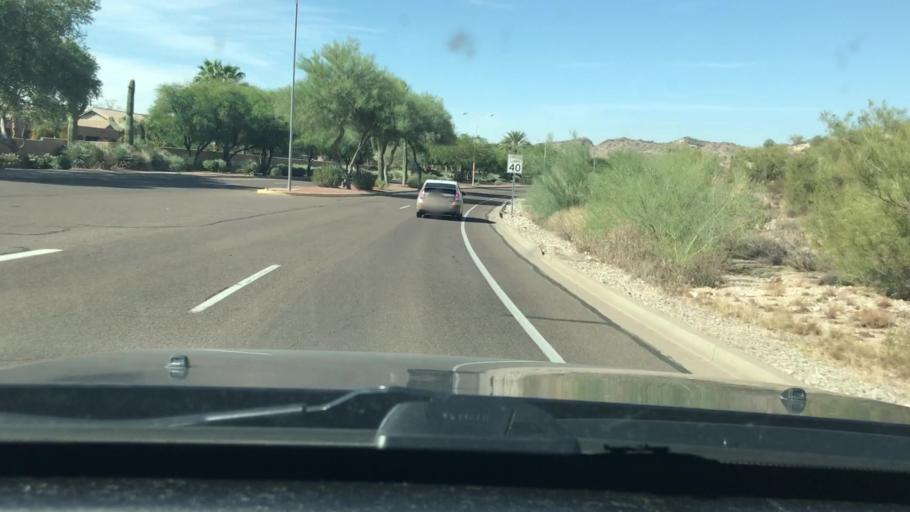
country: US
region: Arizona
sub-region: Maricopa County
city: Guadalupe
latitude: 33.3127
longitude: -112.0189
